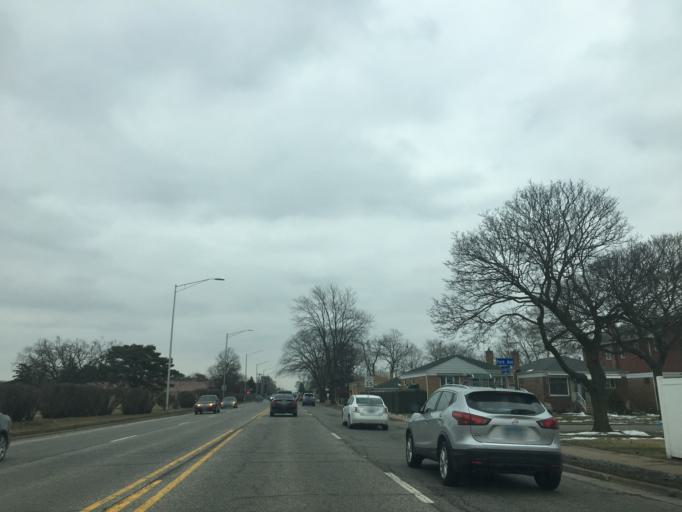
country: US
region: Illinois
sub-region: Cook County
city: North Riverside
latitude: 41.8501
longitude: -87.8200
